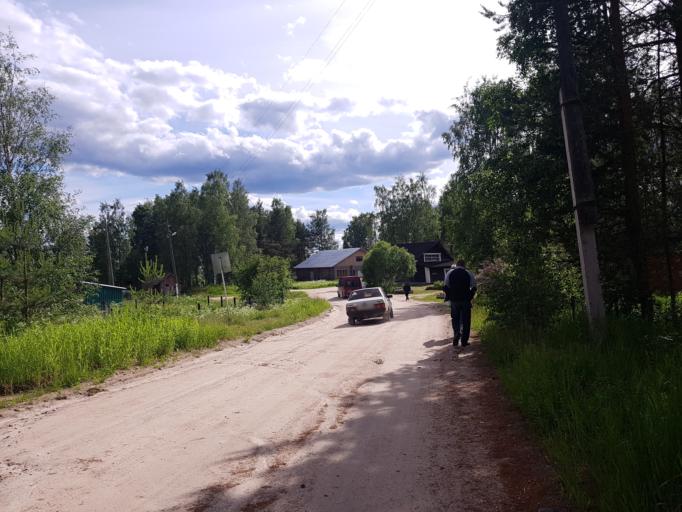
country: RU
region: Republic of Karelia
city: Kostomuksha
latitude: 64.9536
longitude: 30.5584
